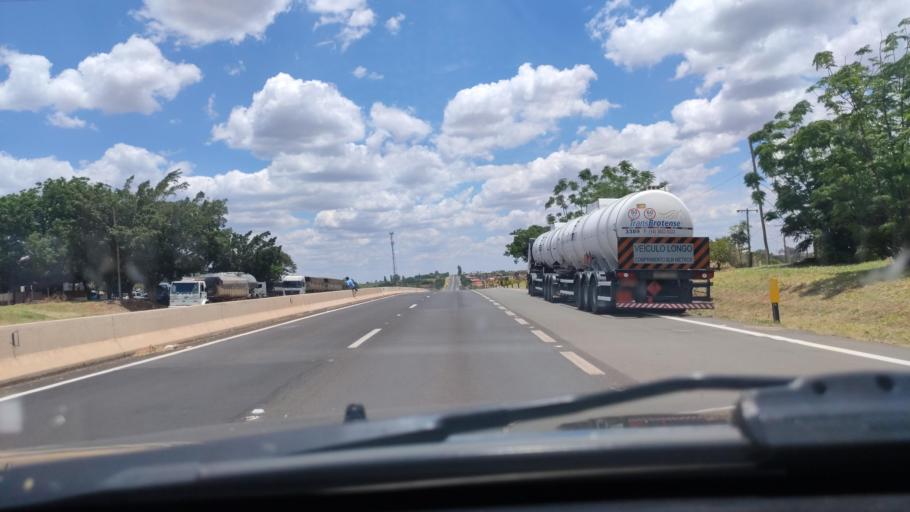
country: BR
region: Sao Paulo
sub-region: Duartina
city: Duartina
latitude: -22.6909
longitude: -49.4228
